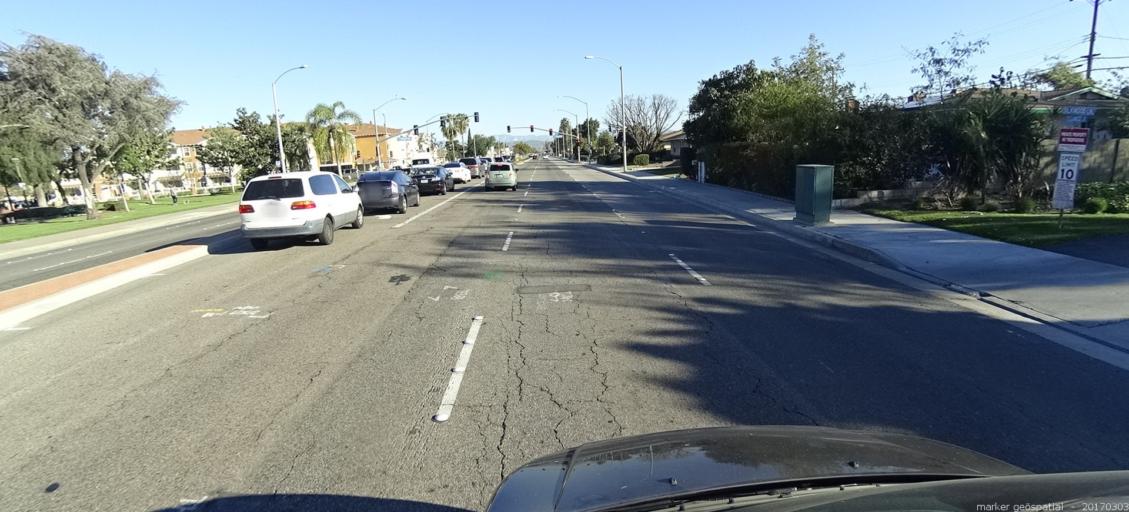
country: US
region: California
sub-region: Orange County
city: Anaheim
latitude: 33.8270
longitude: -117.8892
